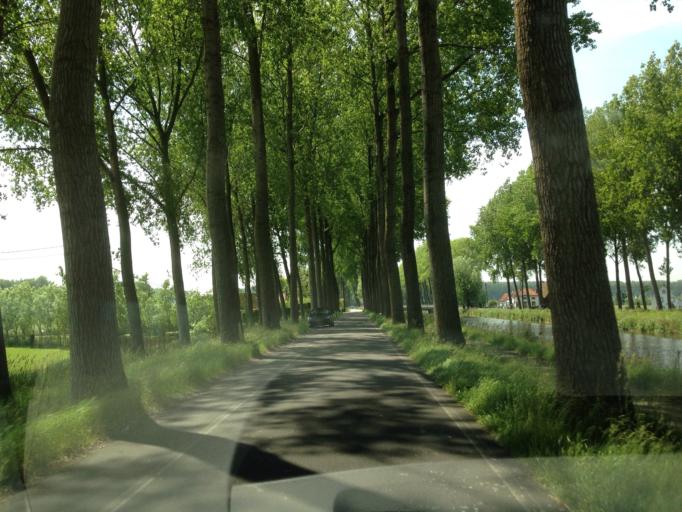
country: BE
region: Flanders
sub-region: Provincie West-Vlaanderen
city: Damme
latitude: 51.2740
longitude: 3.3065
